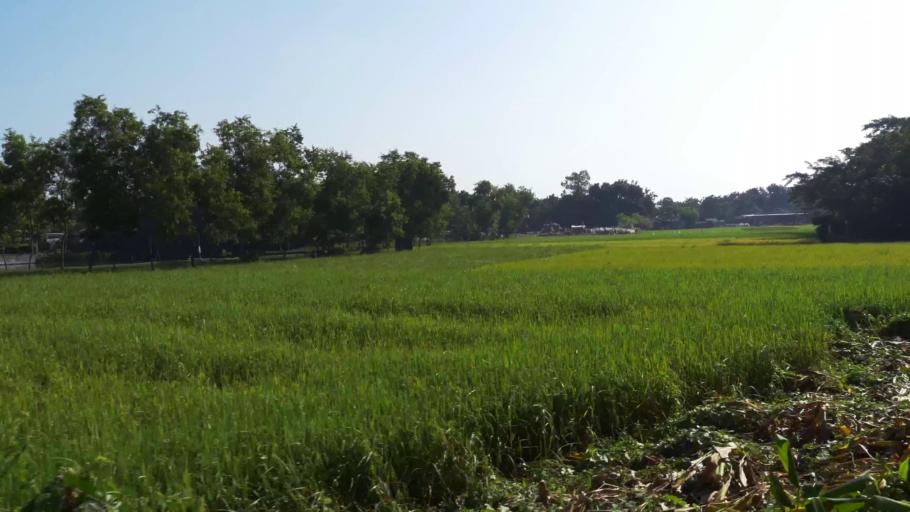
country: BD
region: Dhaka
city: Muktagacha
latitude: 24.8122
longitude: 90.2919
